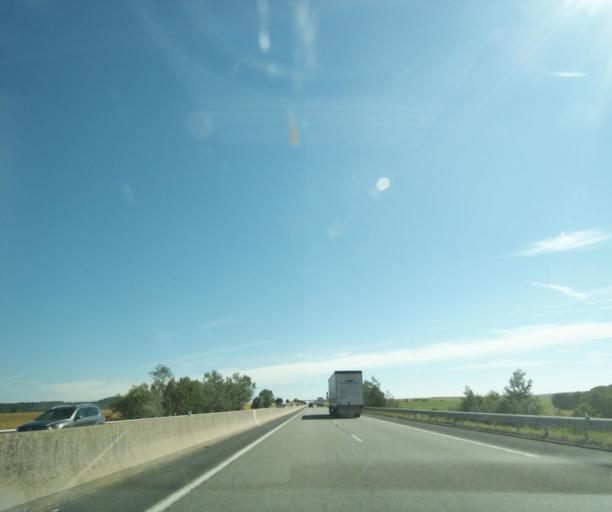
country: FR
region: Lorraine
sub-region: Departement des Vosges
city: Lamarche
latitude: 48.1663
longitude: 5.7114
